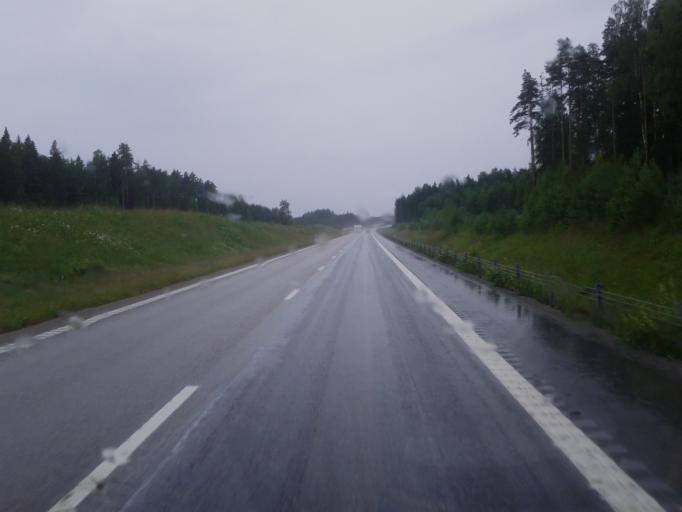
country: SE
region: Uppsala
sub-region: Tierps Kommun
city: Tierp
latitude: 60.2565
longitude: 17.5007
